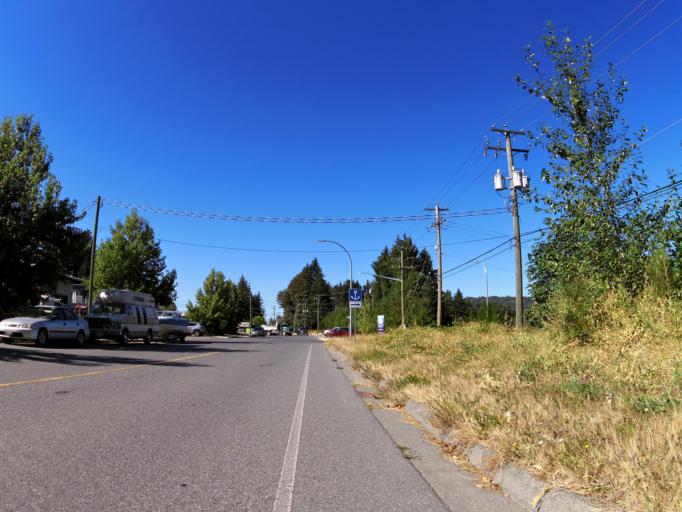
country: CA
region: British Columbia
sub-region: Cowichan Valley Regional District
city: Ladysmith
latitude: 49.0037
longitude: -123.8312
